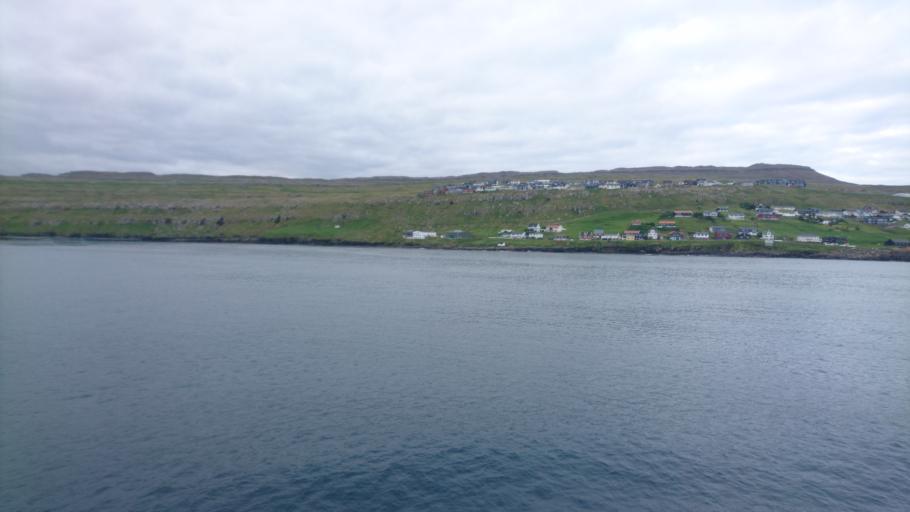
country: FO
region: Streymoy
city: Argir
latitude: 61.9969
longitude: -6.7581
